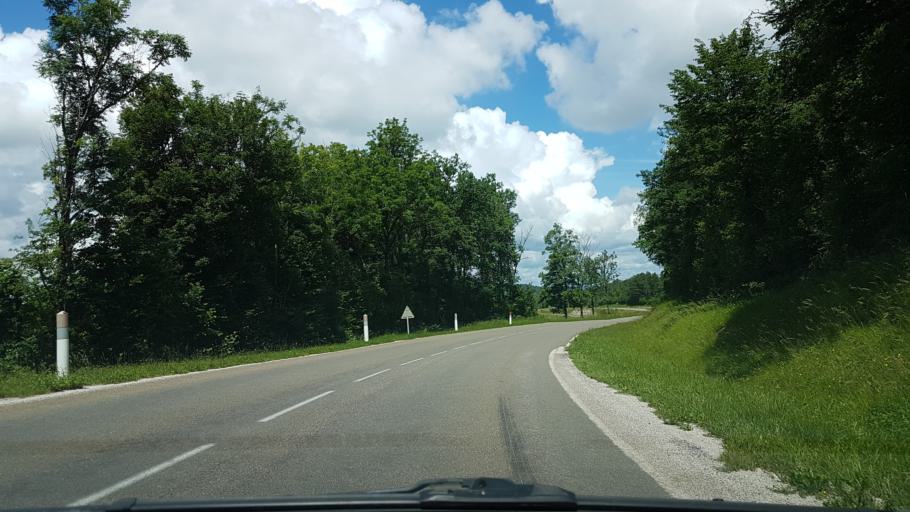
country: FR
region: Franche-Comte
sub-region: Departement du Jura
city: Clairvaux-les-Lacs
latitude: 46.5506
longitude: 5.7446
